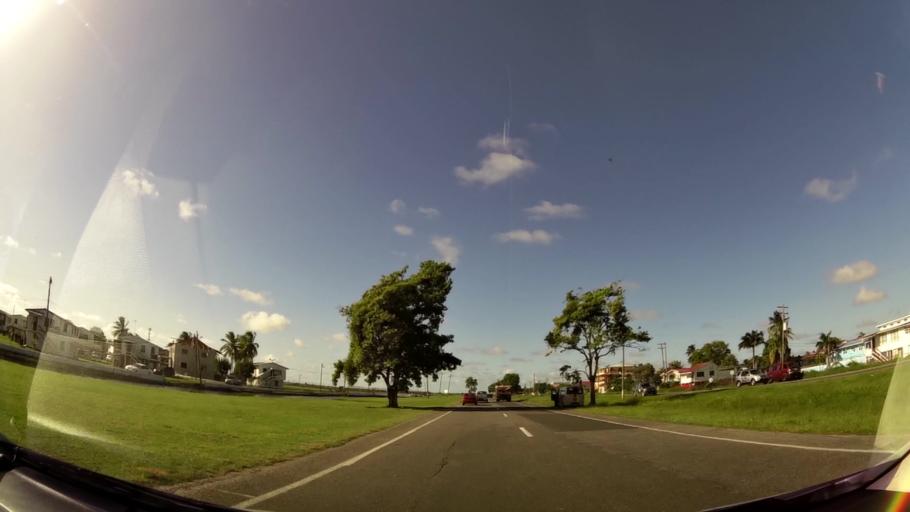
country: GY
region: Demerara-Mahaica
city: Georgetown
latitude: 6.8211
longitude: -58.1446
